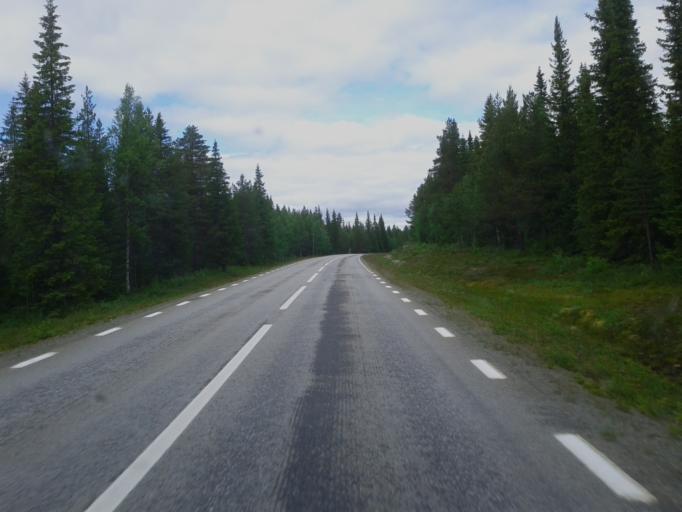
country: SE
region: Vaesterbotten
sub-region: Storumans Kommun
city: Fristad
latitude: 65.3661
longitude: 16.5237
